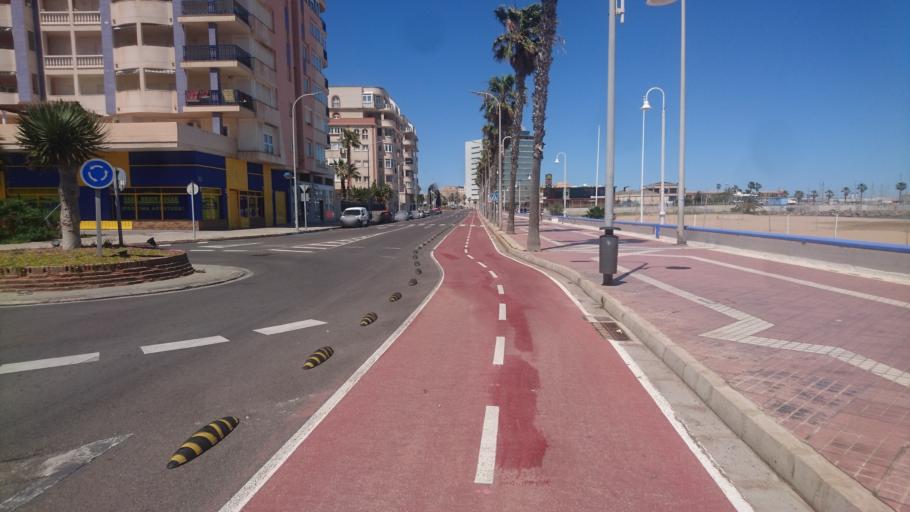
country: ES
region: Melilla
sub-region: Melilla
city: Melilla
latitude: 35.2864
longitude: -2.9382
